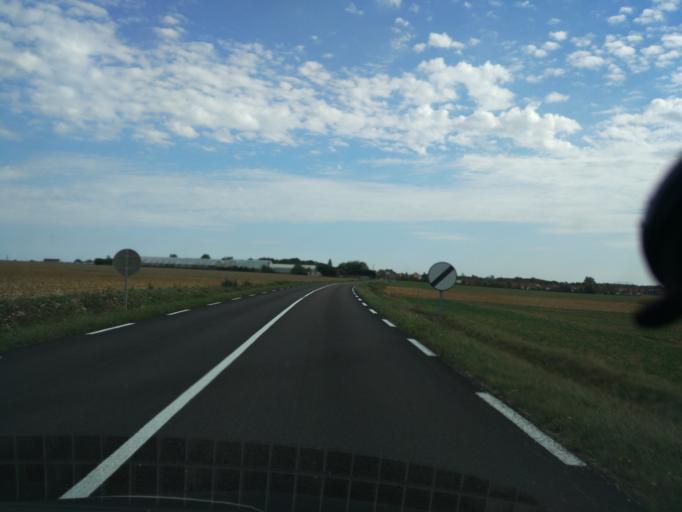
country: FR
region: Ile-de-France
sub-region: Departement de l'Essonne
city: Gometz-la-Ville
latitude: 48.6739
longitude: 2.1122
